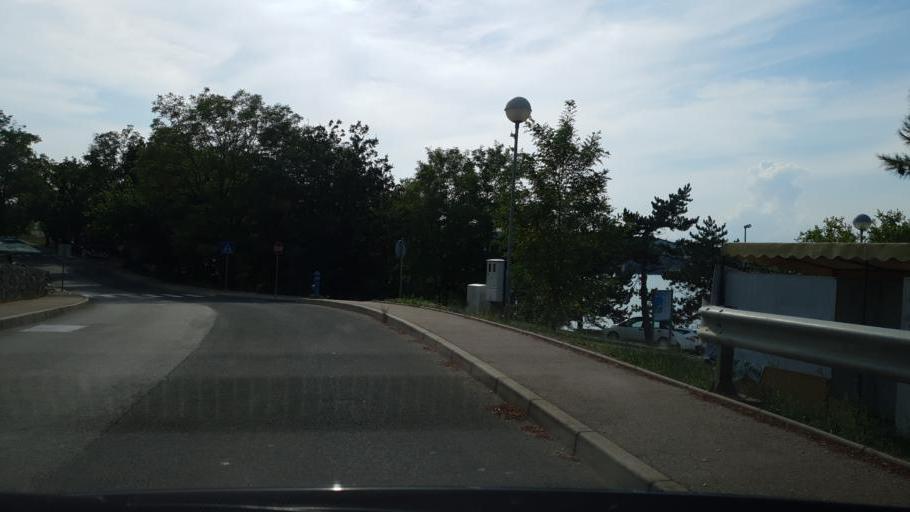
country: HR
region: Primorsko-Goranska
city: Njivice
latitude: 45.1504
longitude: 14.6093
